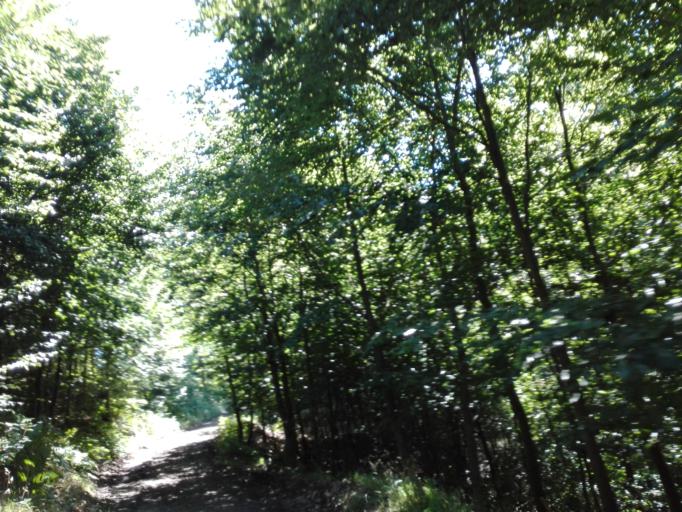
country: DK
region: Central Jutland
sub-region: Odder Kommune
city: Odder
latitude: 55.9511
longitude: 10.1386
